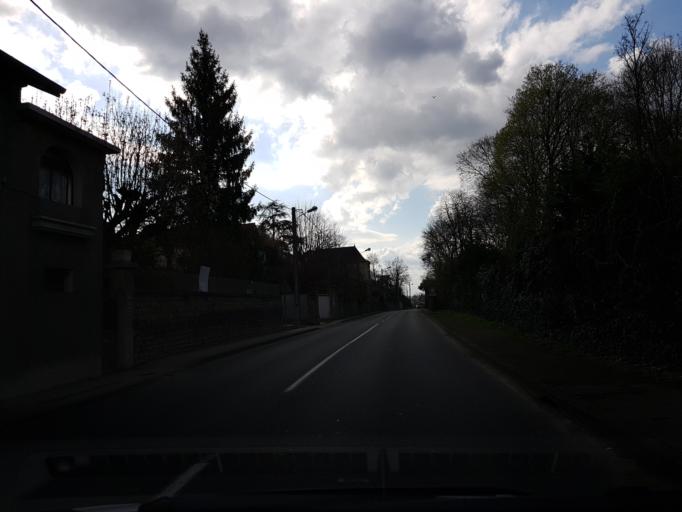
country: FR
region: Rhone-Alpes
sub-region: Departement de l'Ain
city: Trevoux
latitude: 45.9445
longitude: 4.7610
